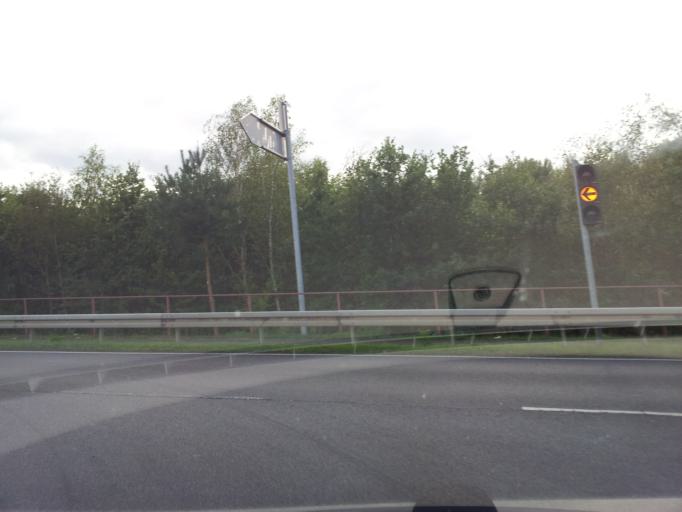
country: DE
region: Brandenburg
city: Schwarzheide
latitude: 51.4676
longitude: 13.8602
